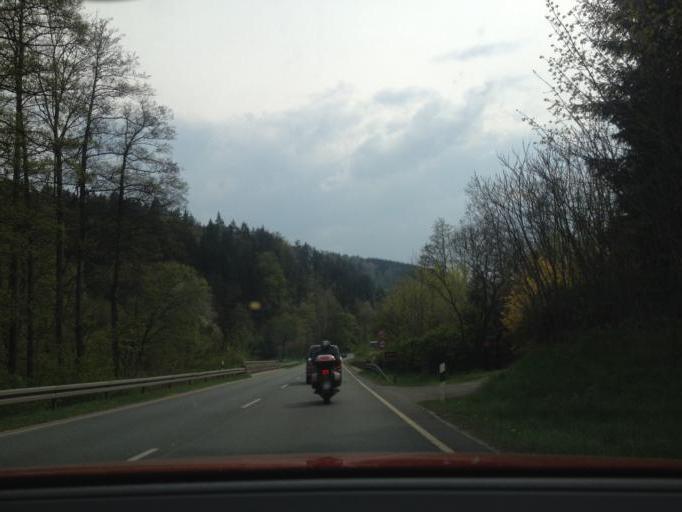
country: DE
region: Bavaria
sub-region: Upper Franconia
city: Goldkronach
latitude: 50.0319
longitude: 11.7083
